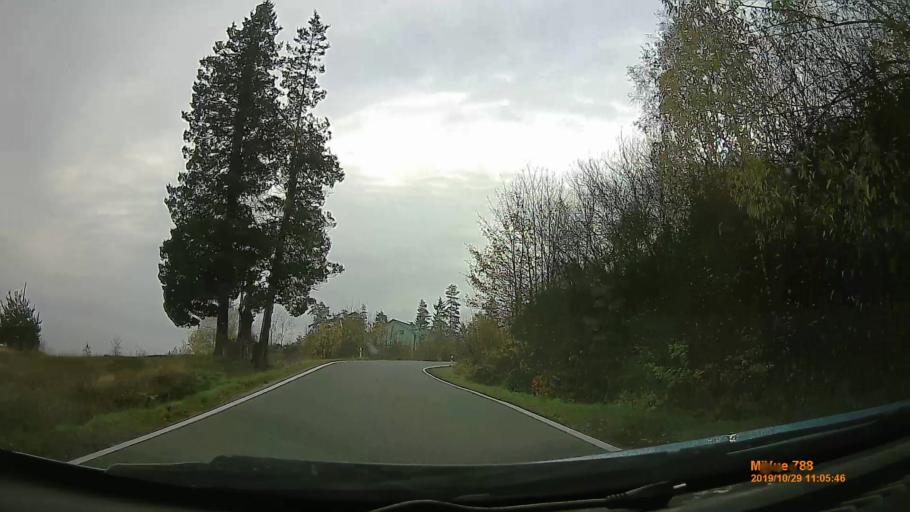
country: PL
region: Lower Silesian Voivodeship
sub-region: Powiat klodzki
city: Szczytna
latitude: 50.4677
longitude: 16.4770
